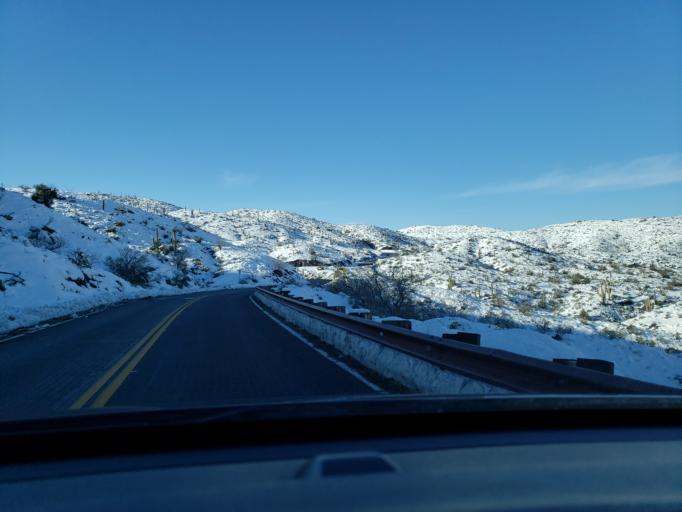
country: US
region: Arizona
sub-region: Maricopa County
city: Carefree
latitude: 33.8889
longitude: -111.8193
